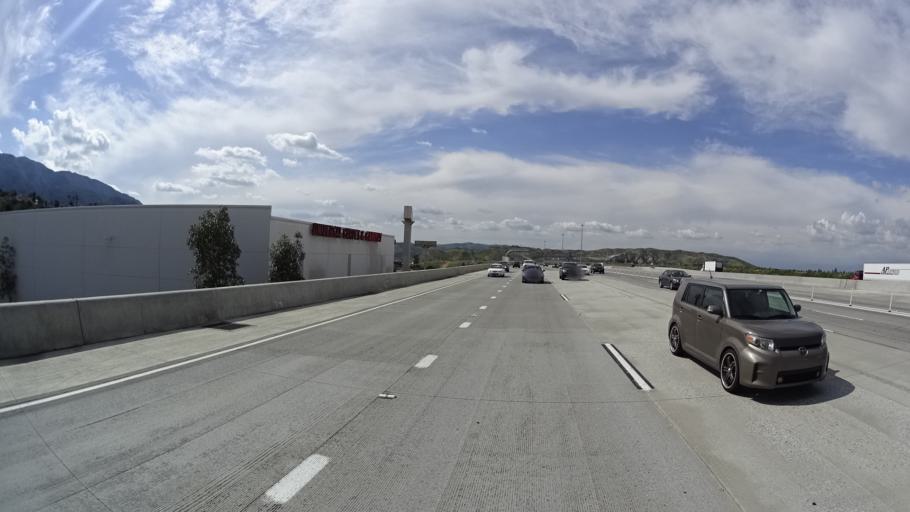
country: US
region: California
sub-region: Riverside County
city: Corona
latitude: 33.8832
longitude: -117.6266
